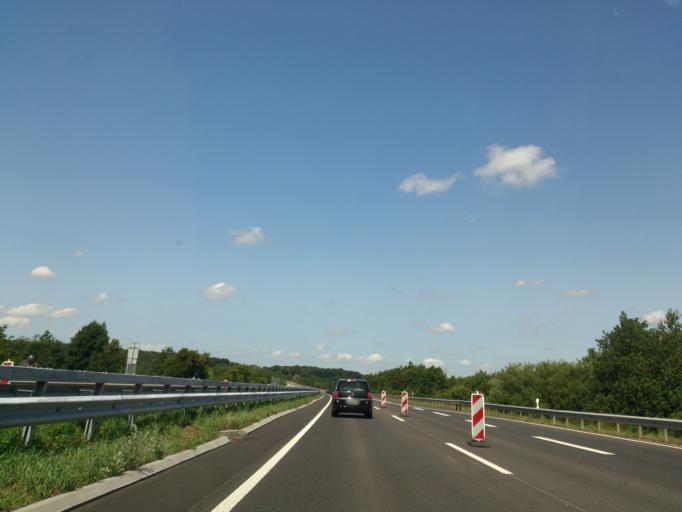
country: DE
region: Schleswig-Holstein
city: Arkebek
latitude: 54.1400
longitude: 9.2492
